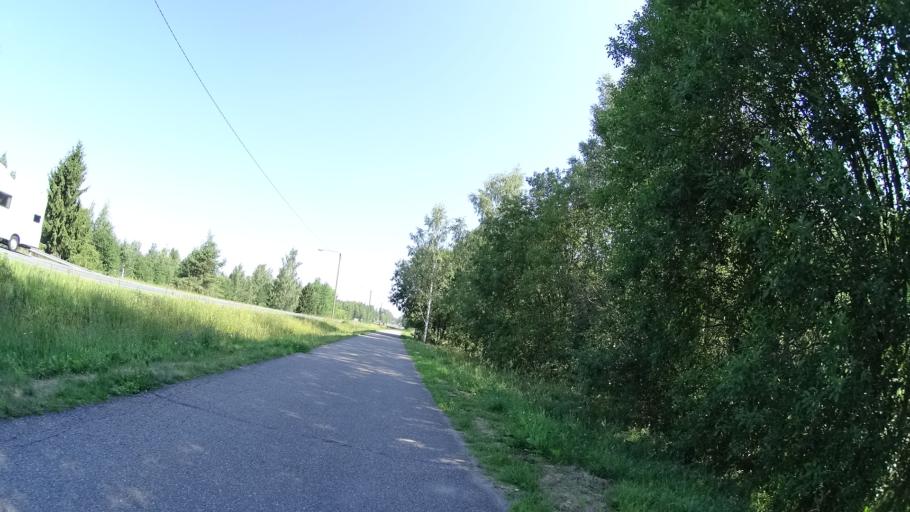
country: FI
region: Uusimaa
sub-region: Helsinki
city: Kerava
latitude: 60.3375
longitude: 25.1250
